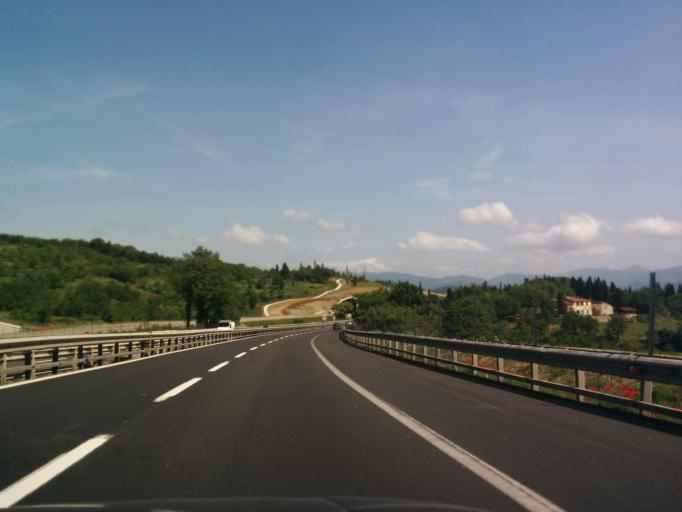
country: IT
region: Tuscany
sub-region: Province of Florence
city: Cavallina
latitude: 43.9567
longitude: 11.2090
